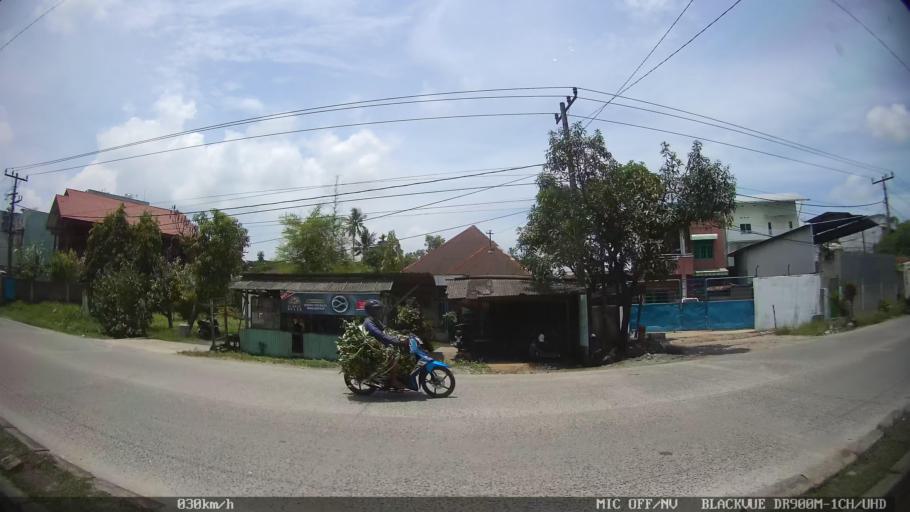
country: ID
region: North Sumatra
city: Labuhan Deli
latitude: 3.7206
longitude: 98.6804
